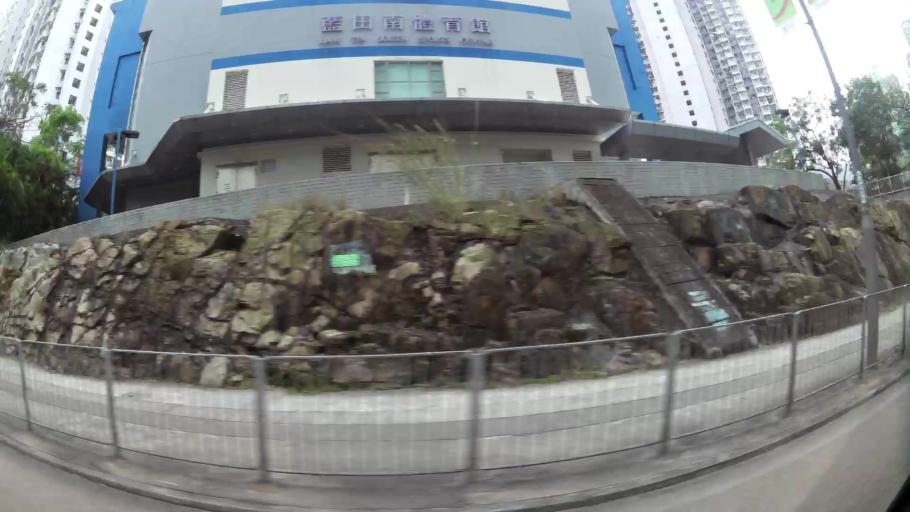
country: HK
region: Kowloon City
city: Kowloon
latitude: 22.3036
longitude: 114.2384
